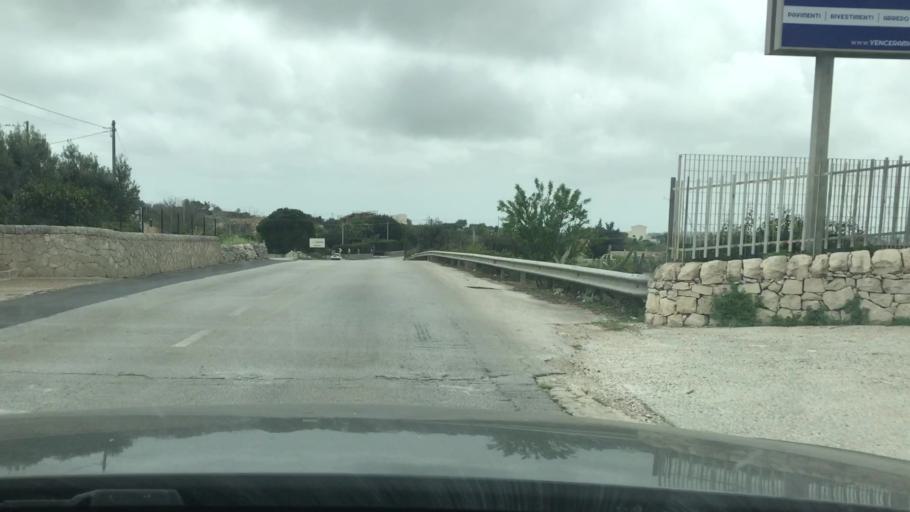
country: IT
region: Sicily
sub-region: Ragusa
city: Modica
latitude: 36.8199
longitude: 14.7451
